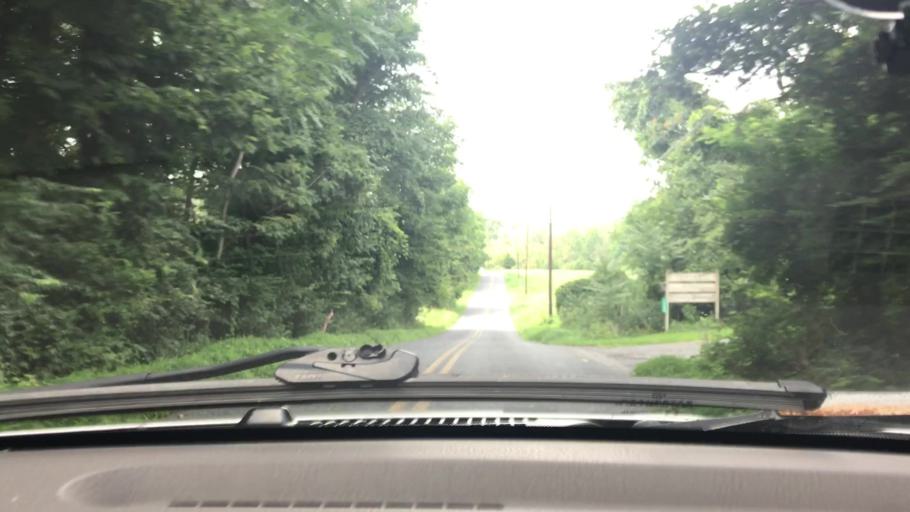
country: US
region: Pennsylvania
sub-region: Lancaster County
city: Elizabethtown
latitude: 40.1698
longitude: -76.6194
